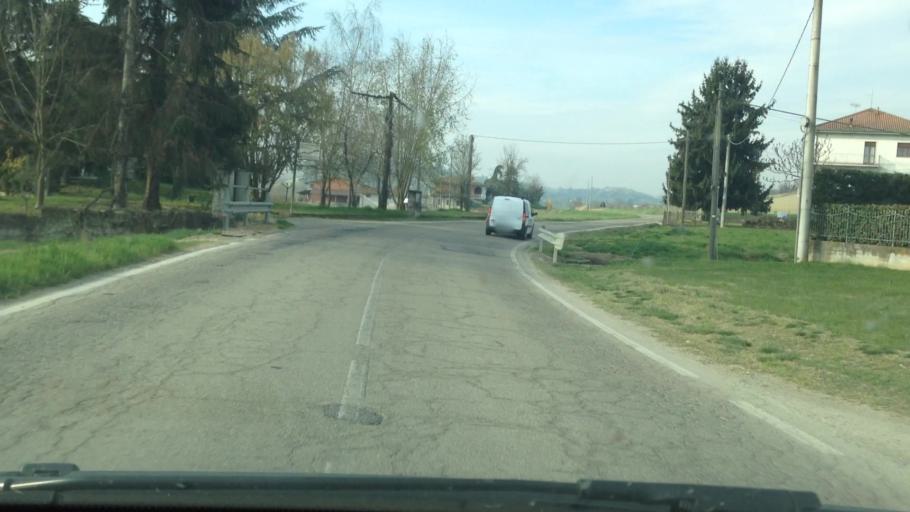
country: IT
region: Piedmont
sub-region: Provincia di Asti
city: San Damiano d'Asti
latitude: 44.8148
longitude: 8.0441
